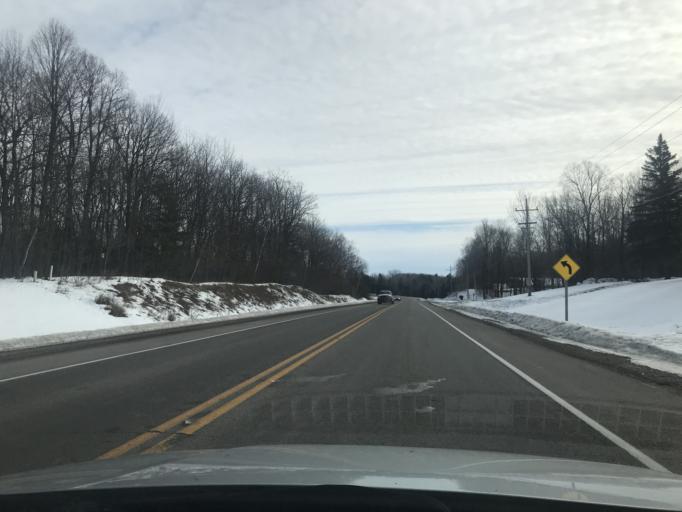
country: US
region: Wisconsin
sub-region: Oconto County
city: Oconto Falls
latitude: 44.8897
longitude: -88.1669
